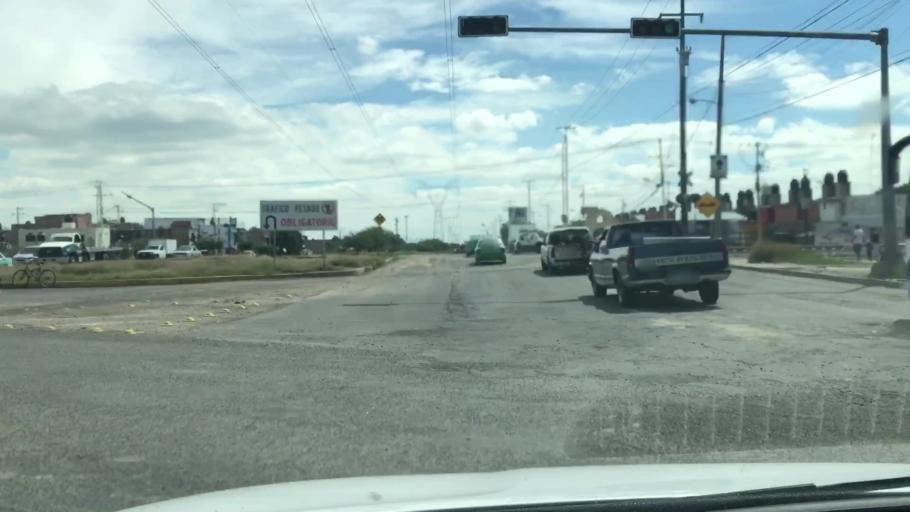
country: MX
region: Guanajuato
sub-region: Celaya
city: La Trinidad
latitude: 20.5496
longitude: -100.7939
